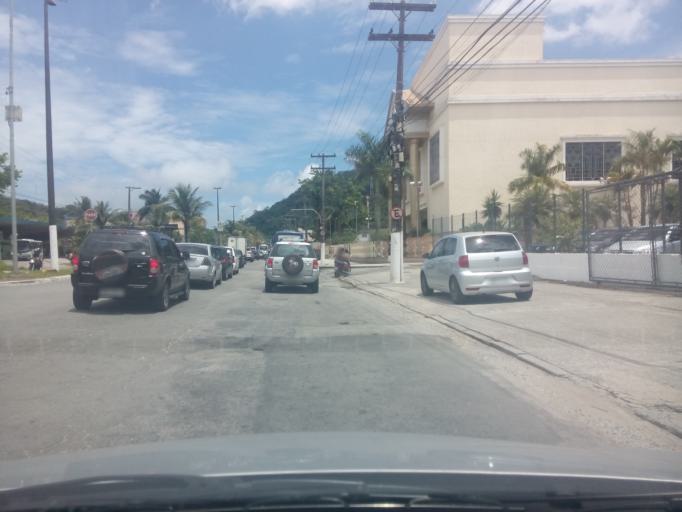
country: BR
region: Sao Paulo
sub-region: Guaruja
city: Guaruja
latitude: -23.9838
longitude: -46.2677
